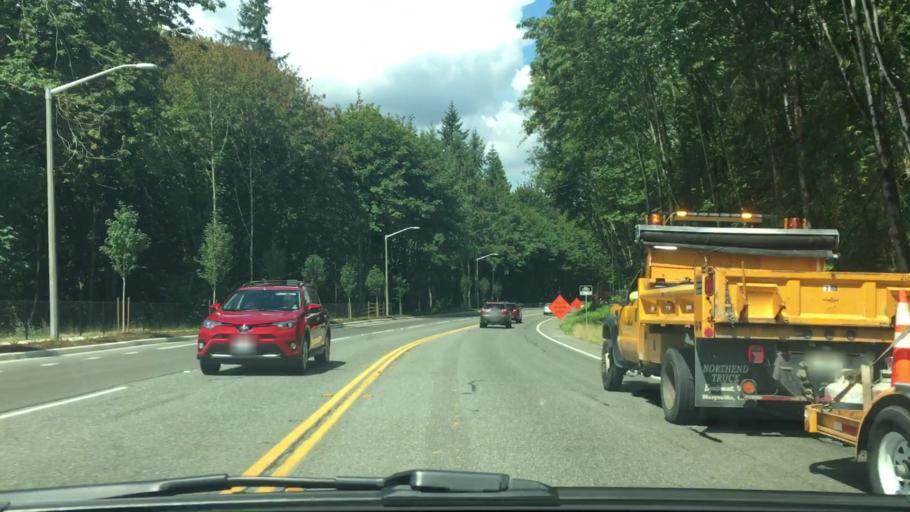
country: US
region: Washington
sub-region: King County
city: City of Sammamish
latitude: 47.5678
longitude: -122.0449
